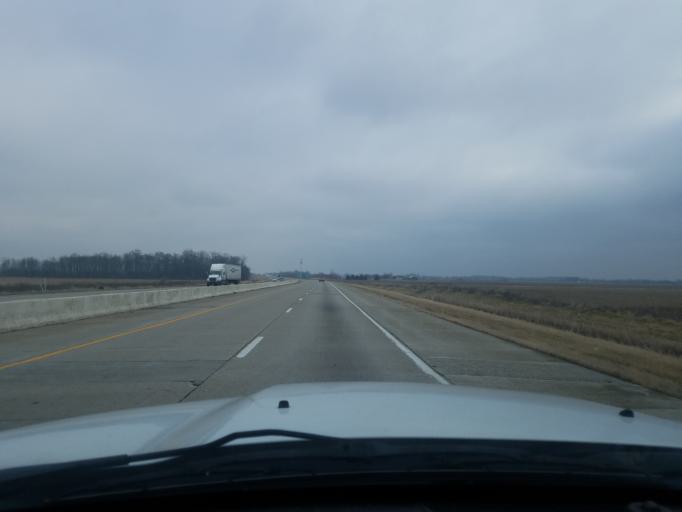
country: US
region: Indiana
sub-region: Wells County
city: Ossian
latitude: 40.9526
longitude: -85.1985
